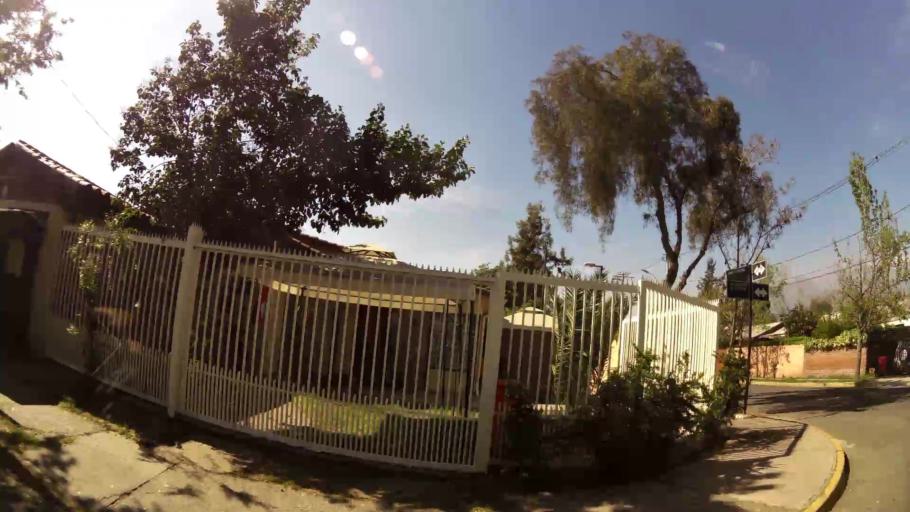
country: CL
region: Santiago Metropolitan
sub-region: Provincia de Santiago
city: Villa Presidente Frei, Nunoa, Santiago, Chile
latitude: -33.4935
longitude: -70.5787
